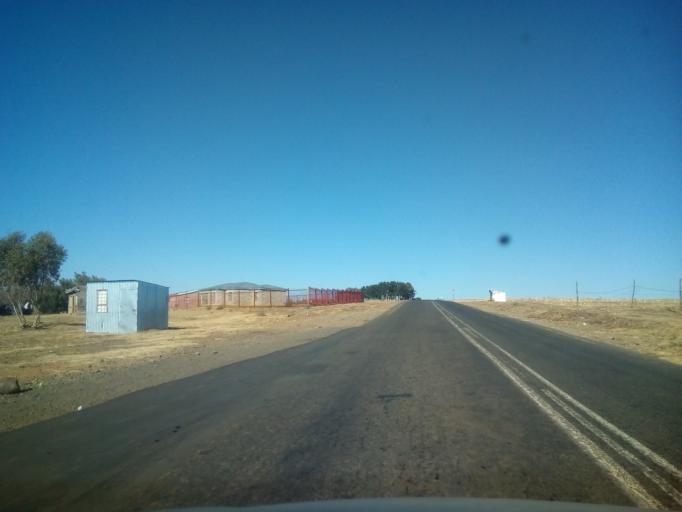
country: LS
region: Maseru
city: Maseru
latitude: -29.2939
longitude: 27.6187
